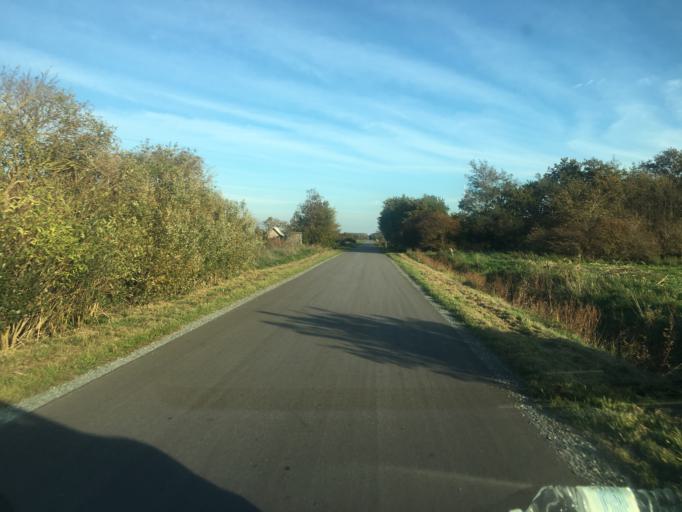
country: DE
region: Schleswig-Holstein
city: Ladelund
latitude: 54.8951
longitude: 9.0370
